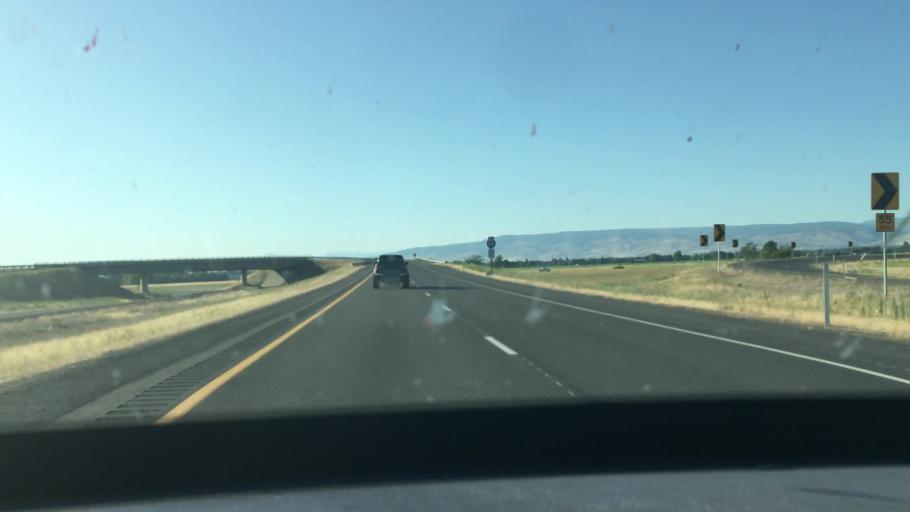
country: US
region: Washington
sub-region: Kittitas County
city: Ellensburg
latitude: 46.9715
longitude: -120.5072
